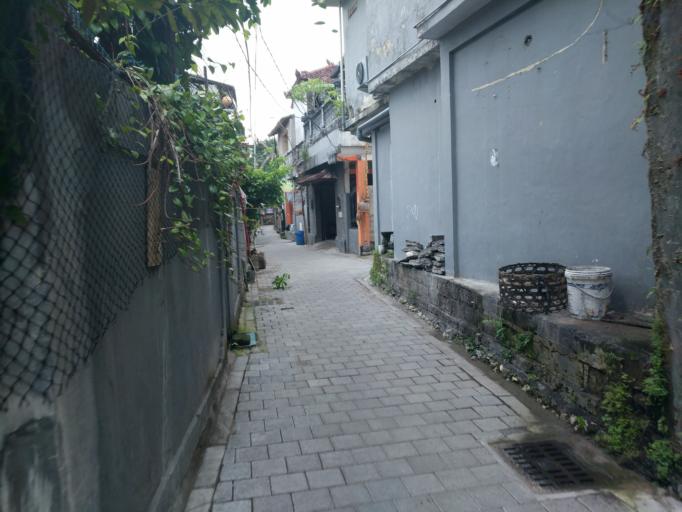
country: ID
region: Bali
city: Jabajero
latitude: -8.7391
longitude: 115.1651
